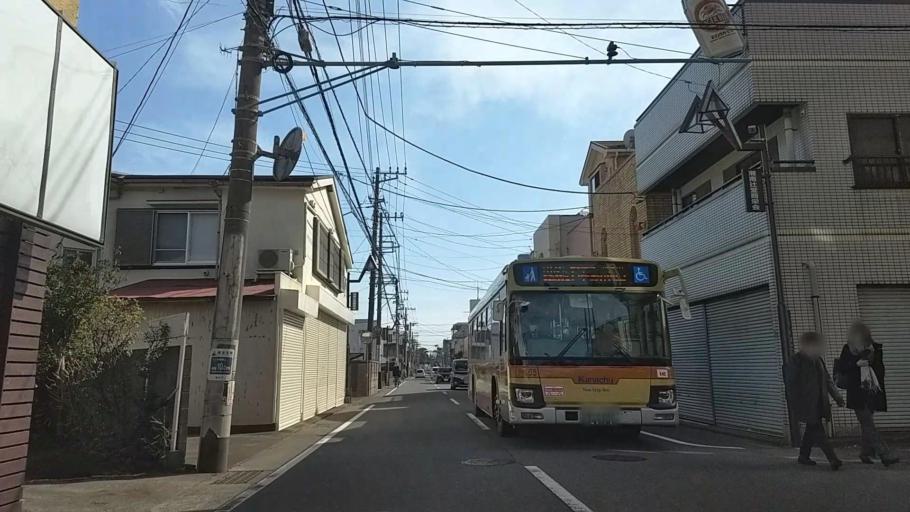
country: JP
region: Kanagawa
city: Fujisawa
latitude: 35.3314
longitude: 139.4512
